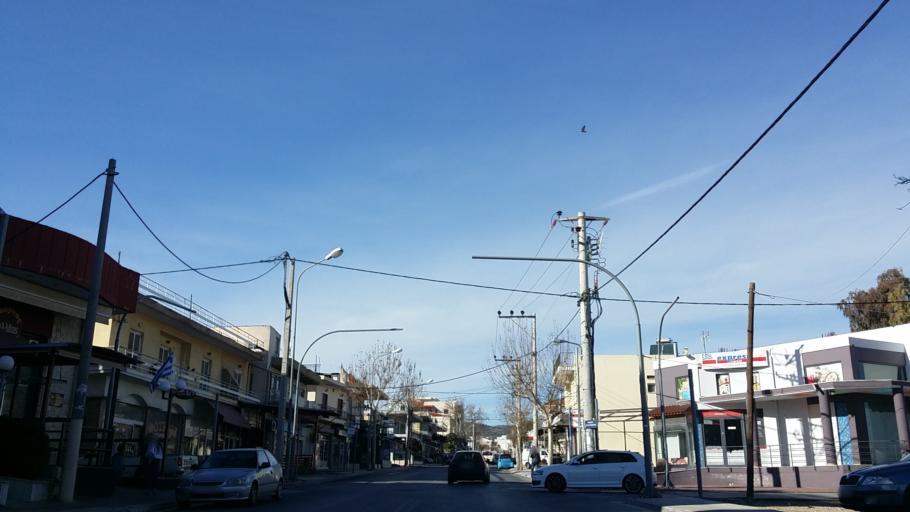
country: GR
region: Attica
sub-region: Nomarchia Dytikis Attikis
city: Ano Liosia
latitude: 38.0812
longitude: 23.6977
